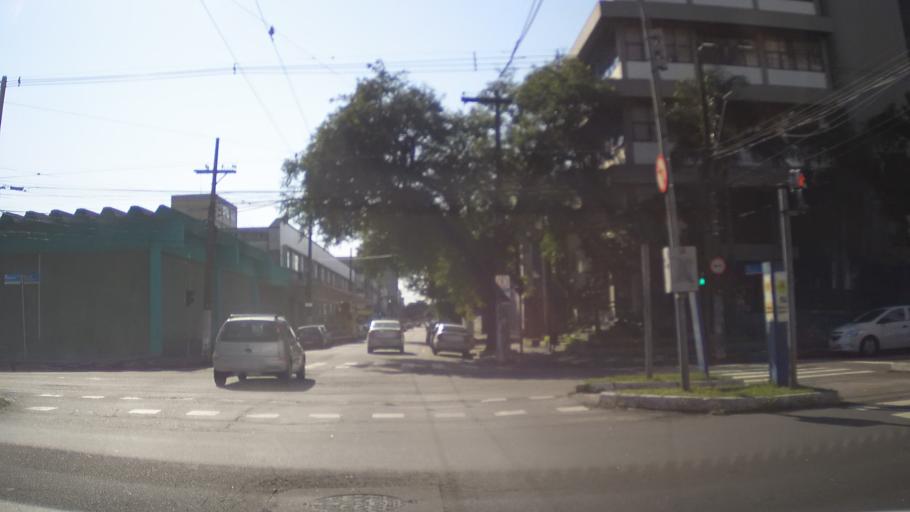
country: BR
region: Sao Paulo
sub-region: Santos
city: Santos
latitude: -23.9441
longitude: -46.3302
